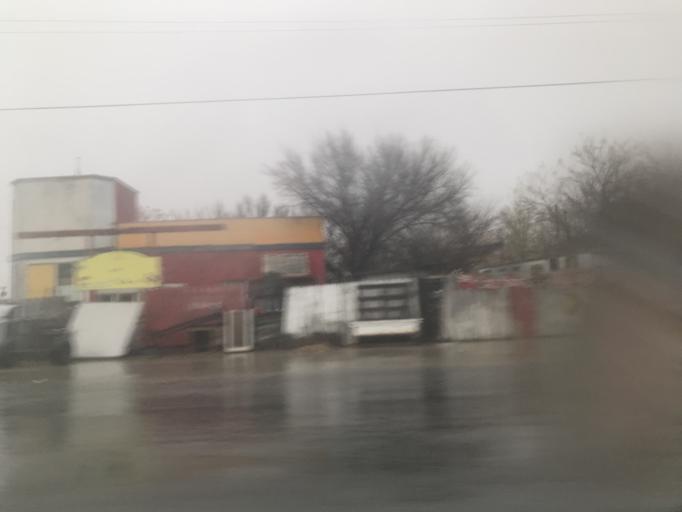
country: US
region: Texas
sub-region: Tom Green County
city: San Angelo
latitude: 31.4522
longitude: -100.4346
